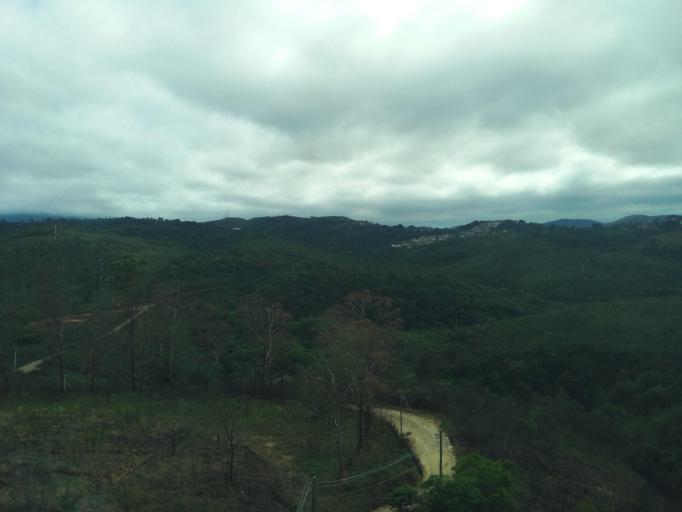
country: BR
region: Minas Gerais
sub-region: Caete
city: Caete
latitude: -19.9103
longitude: -43.6915
